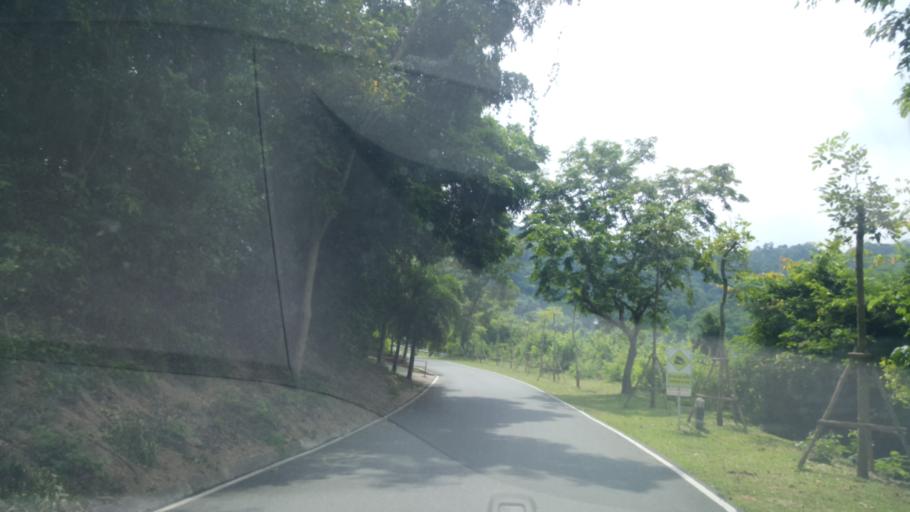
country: TH
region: Chon Buri
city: Ban Bueng
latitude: 13.2113
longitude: 101.0591
